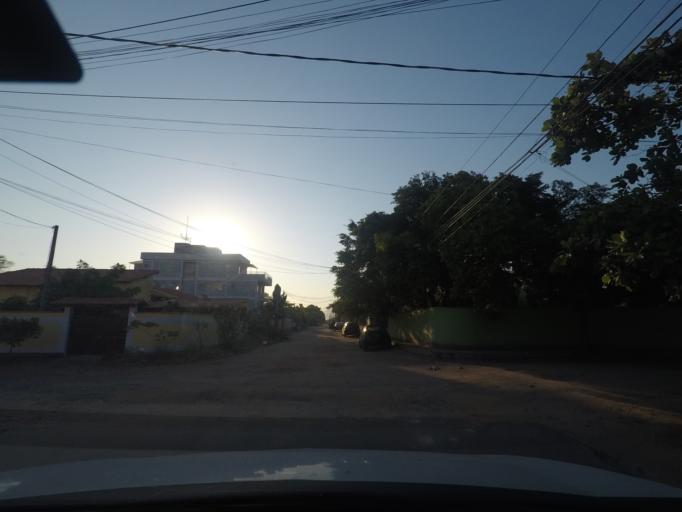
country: BR
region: Rio de Janeiro
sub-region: Marica
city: Marica
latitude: -22.9695
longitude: -42.9279
